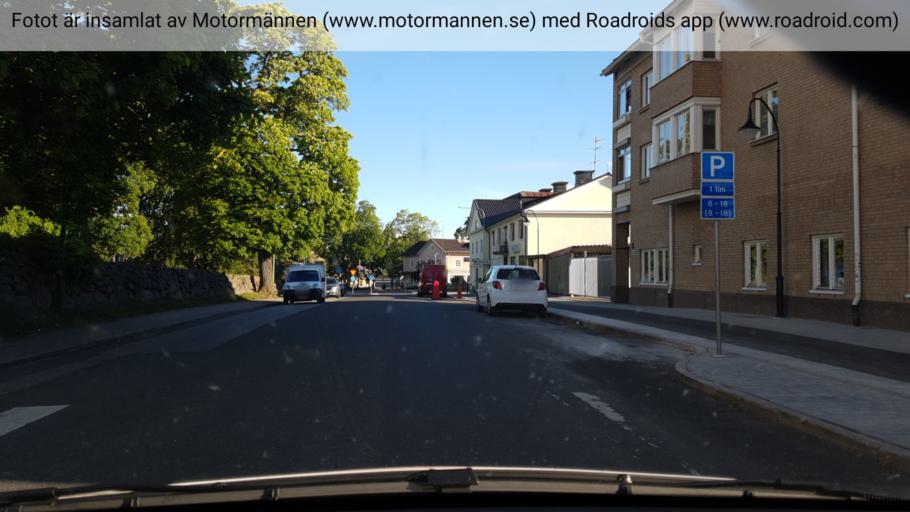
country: SE
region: Vaestra Goetaland
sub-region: Tidaholms Kommun
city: Tidaholm
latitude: 58.1811
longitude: 13.9594
